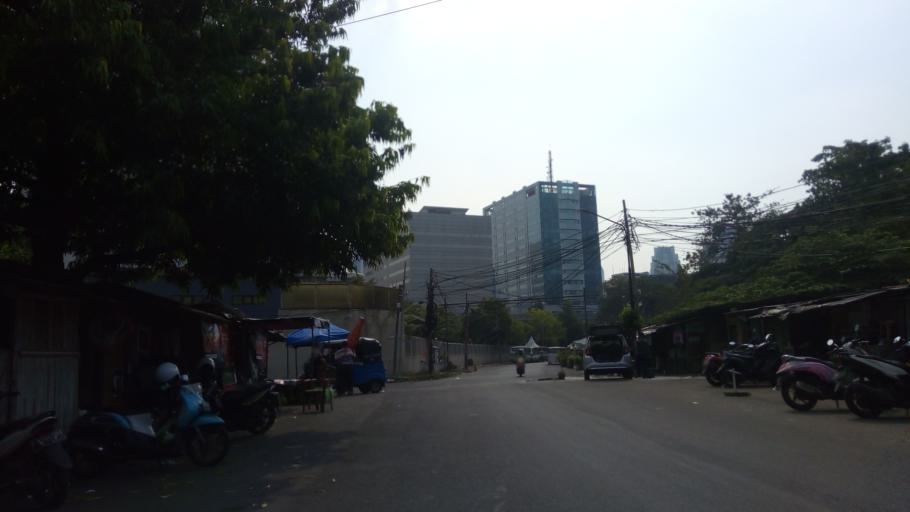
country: ID
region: Jakarta Raya
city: Jakarta
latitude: -6.2124
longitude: 106.8321
